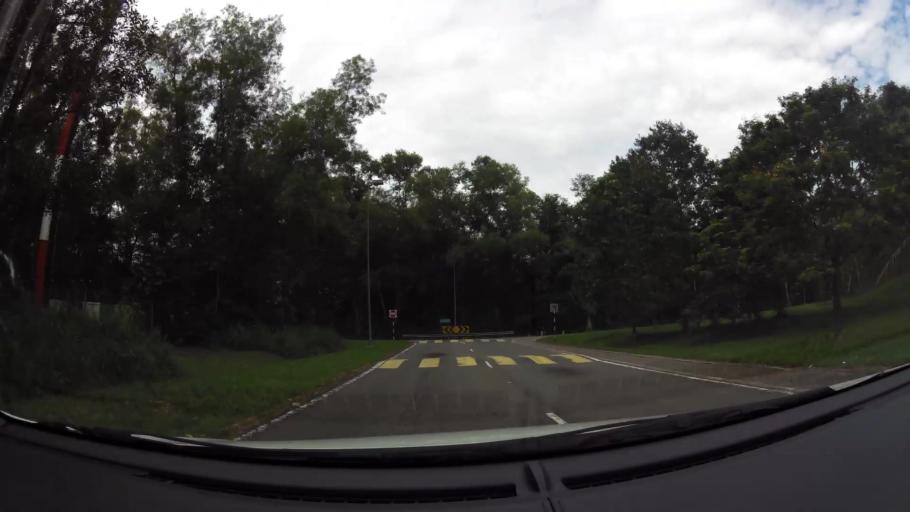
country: BN
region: Brunei and Muara
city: Bandar Seri Begawan
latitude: 4.8805
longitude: 114.9046
